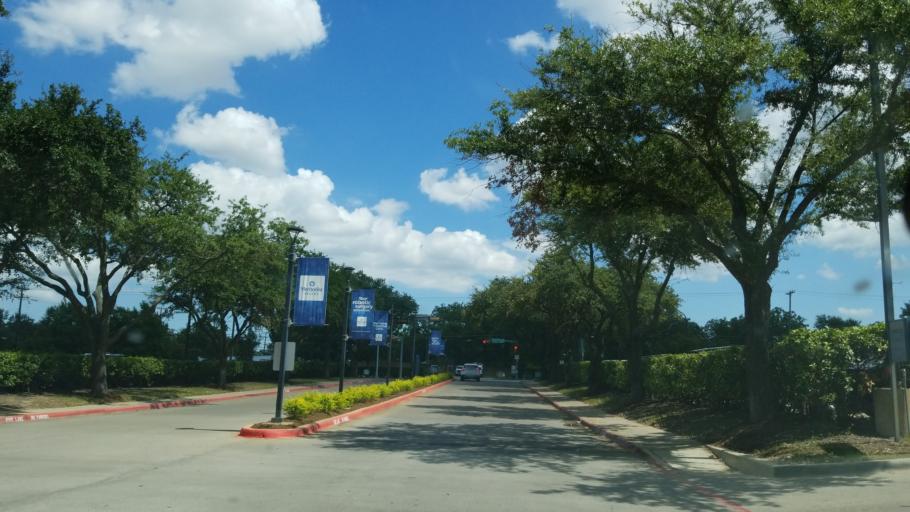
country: US
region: Texas
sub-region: Dallas County
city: Dallas
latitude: 32.7616
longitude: -96.8239
